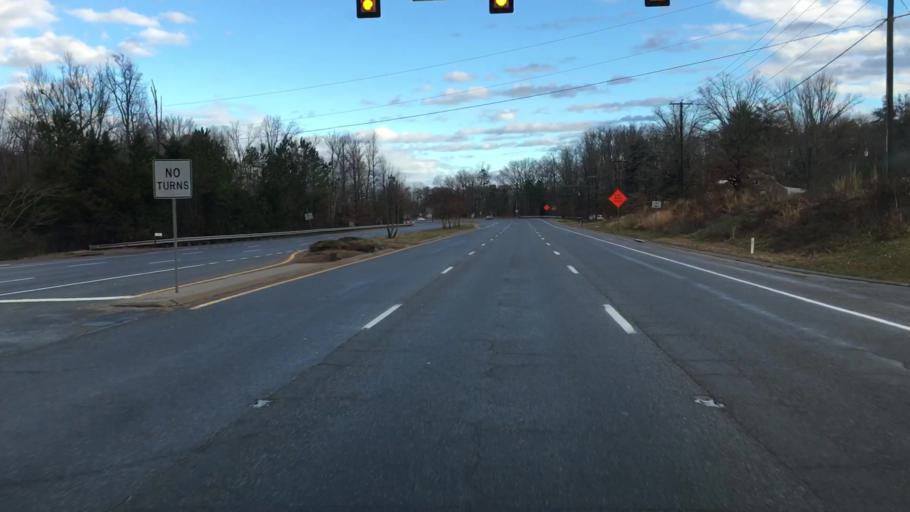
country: US
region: Virginia
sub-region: Chesterfield County
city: Bon Air
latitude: 37.4868
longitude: -77.5971
